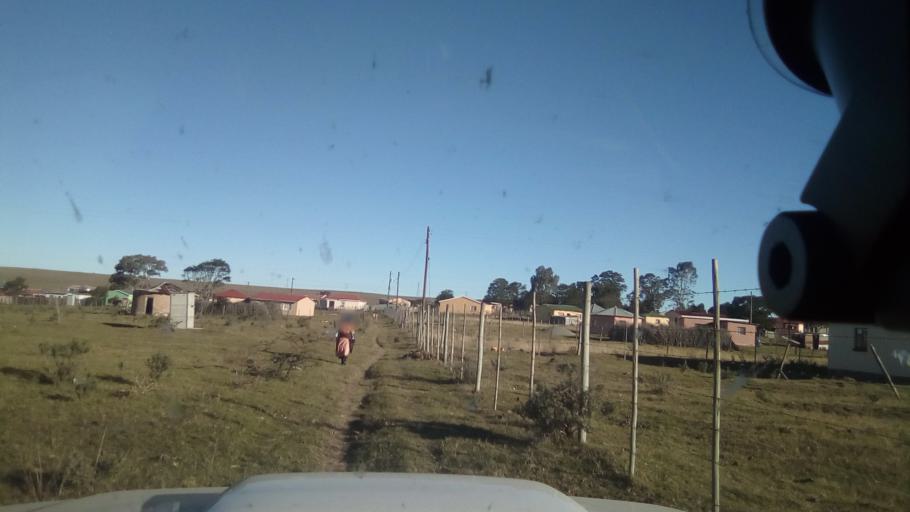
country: ZA
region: Eastern Cape
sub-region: Buffalo City Metropolitan Municipality
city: Bhisho
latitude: -32.9491
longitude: 27.2943
